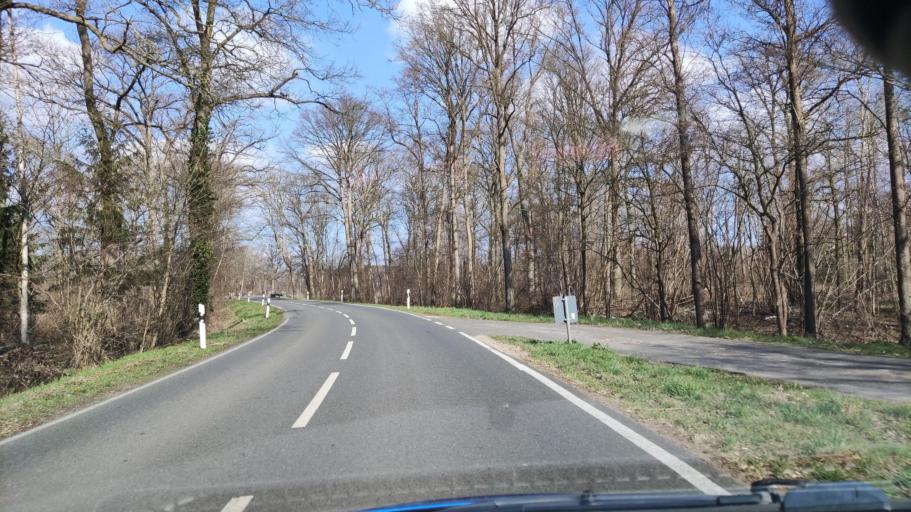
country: DE
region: Lower Saxony
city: Woltersdorf
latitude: 52.9957
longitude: 11.2153
